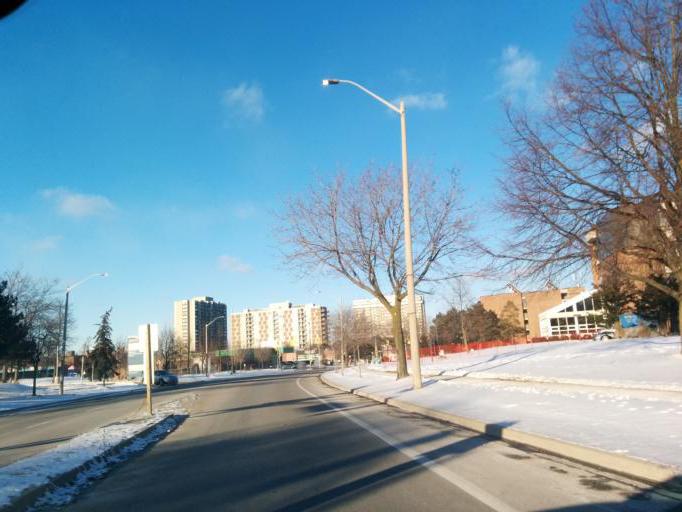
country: CA
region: Ontario
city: Oakville
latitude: 43.5101
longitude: -79.6494
